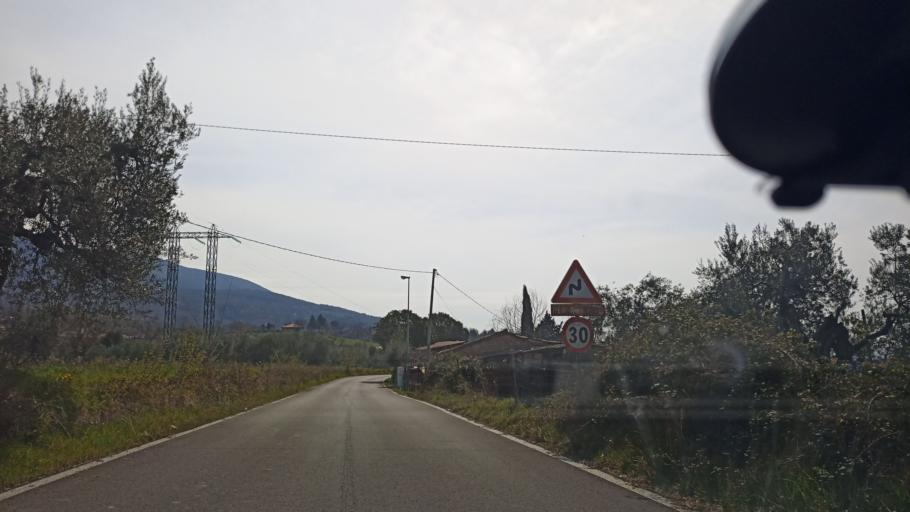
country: IT
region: Latium
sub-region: Provincia di Rieti
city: Montasola
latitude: 42.3671
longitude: 12.6763
